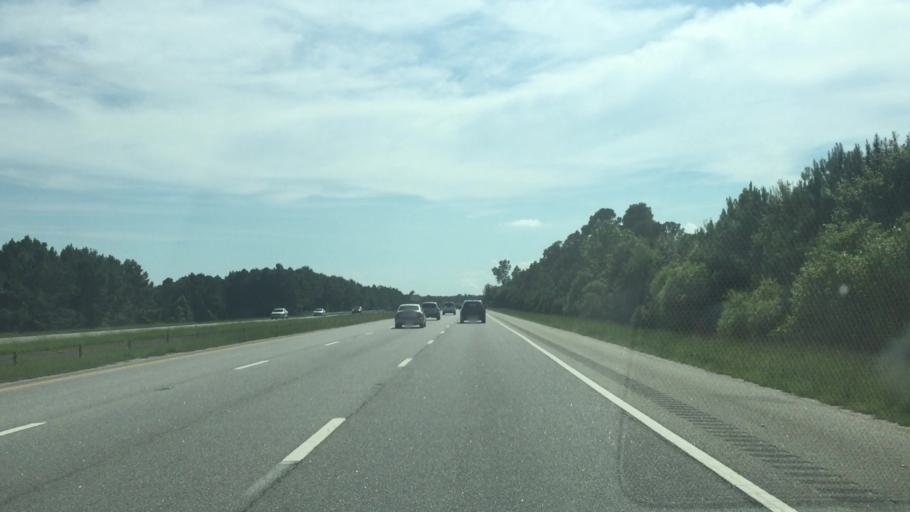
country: US
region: South Carolina
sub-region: Horry County
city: North Myrtle Beach
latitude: 33.8344
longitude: -78.7124
